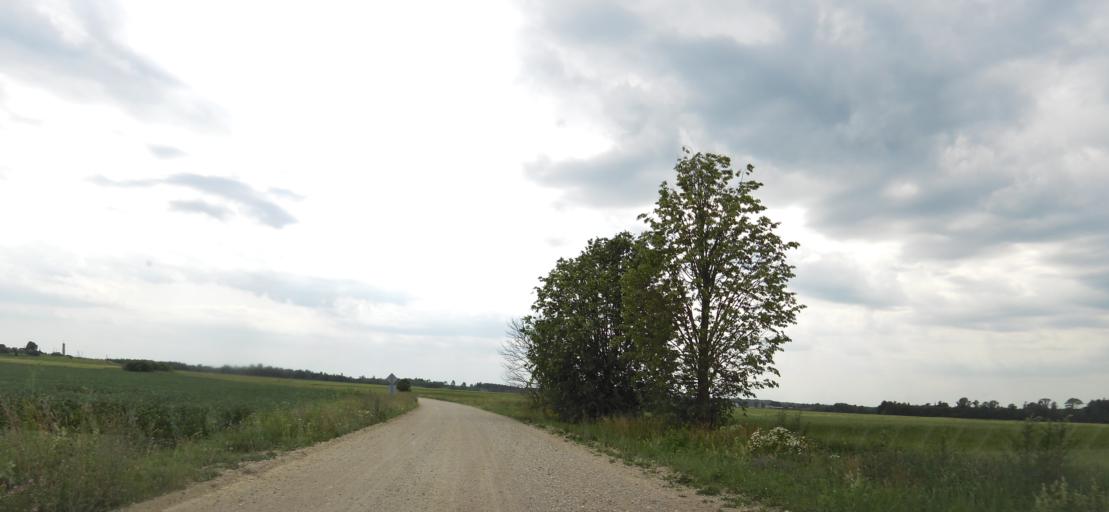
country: LT
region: Panevezys
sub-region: Birzai
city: Birzai
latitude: 56.4216
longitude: 24.8826
